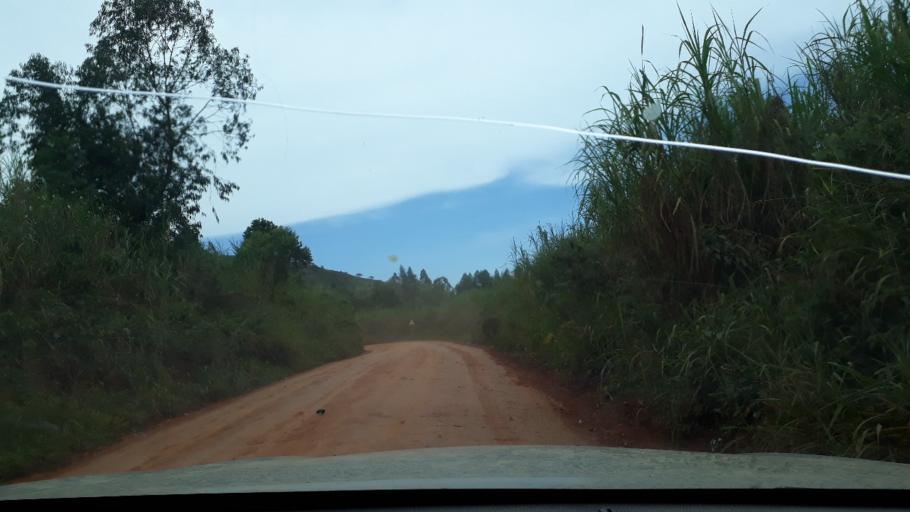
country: CD
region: Eastern Province
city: Bunia
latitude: 1.8015
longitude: 30.3878
